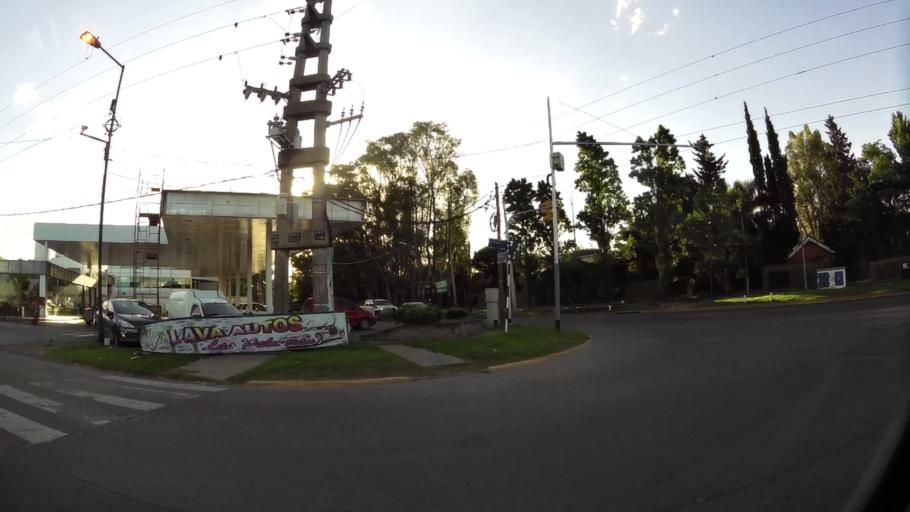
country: AR
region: Buenos Aires
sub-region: Partido de Tigre
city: Tigre
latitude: -34.4660
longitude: -58.5549
